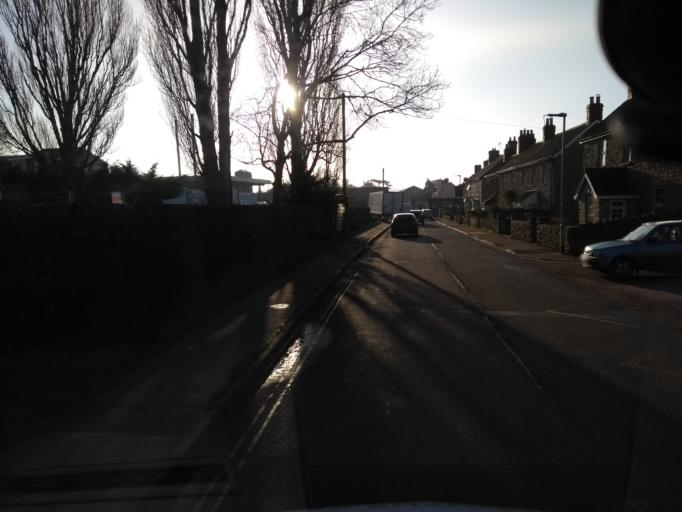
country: GB
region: England
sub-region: Somerset
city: Evercreech
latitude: 51.1498
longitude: -2.5071
